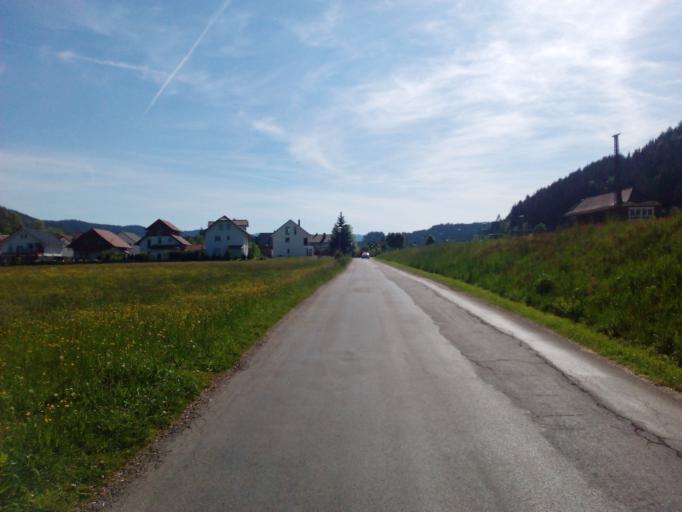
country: DE
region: Baden-Wuerttemberg
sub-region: Freiburg Region
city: Titisee-Neustadt
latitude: 47.9056
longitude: 8.1615
